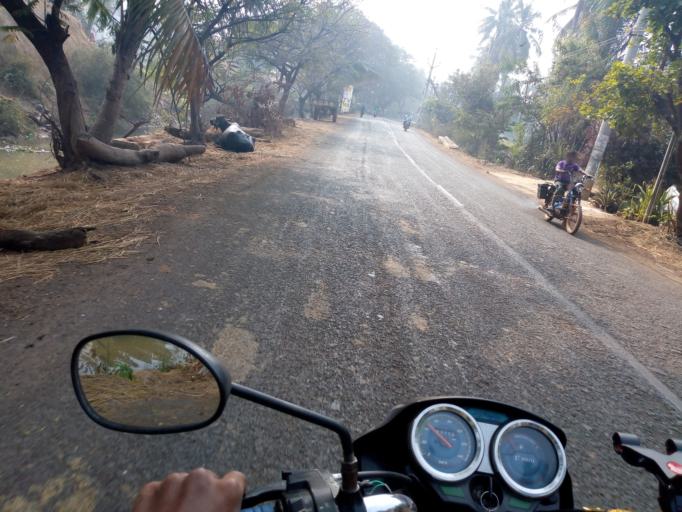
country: IN
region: Andhra Pradesh
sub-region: West Godavari
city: Tadepallegudem
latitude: 16.7784
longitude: 81.4214
